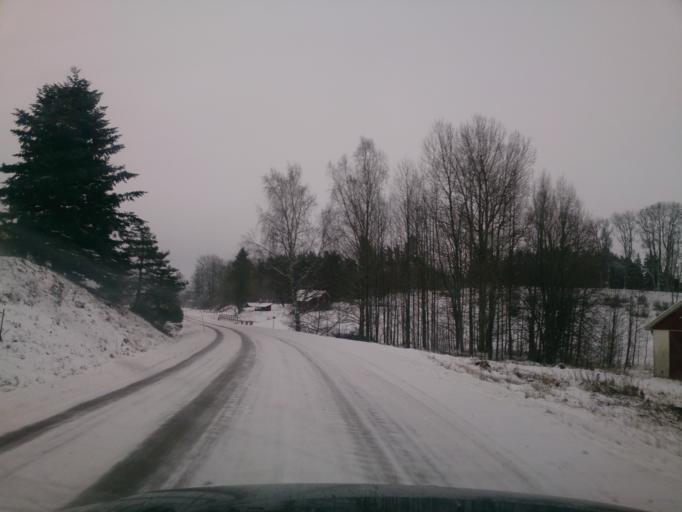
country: SE
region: OEstergoetland
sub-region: Norrkopings Kommun
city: Kimstad
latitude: 58.4173
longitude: 15.9164
